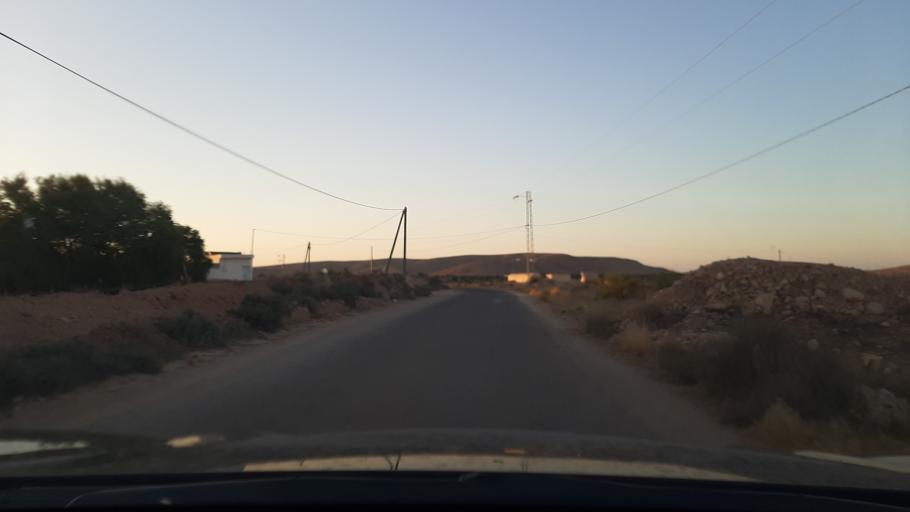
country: TN
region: Qabis
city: Matmata
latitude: 33.5606
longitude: 10.1827
